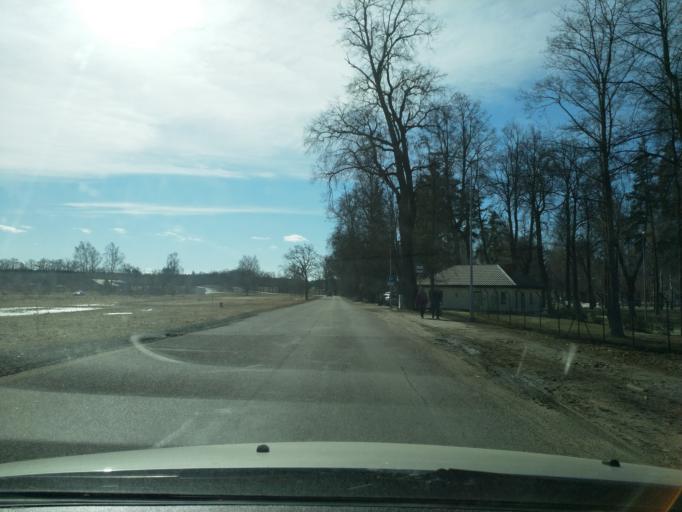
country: LV
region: Valmieras Rajons
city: Valmiera
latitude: 57.5220
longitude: 25.4201
